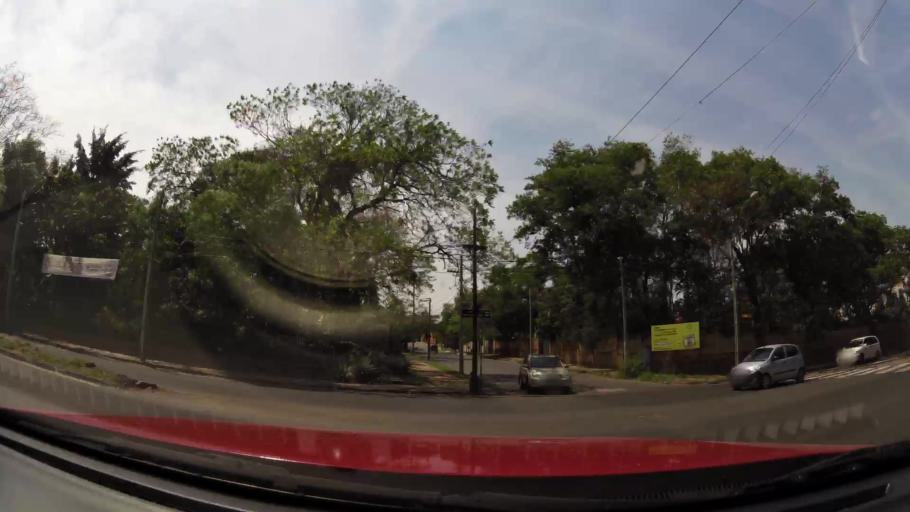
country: PY
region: Asuncion
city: Asuncion
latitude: -25.2798
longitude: -57.5868
